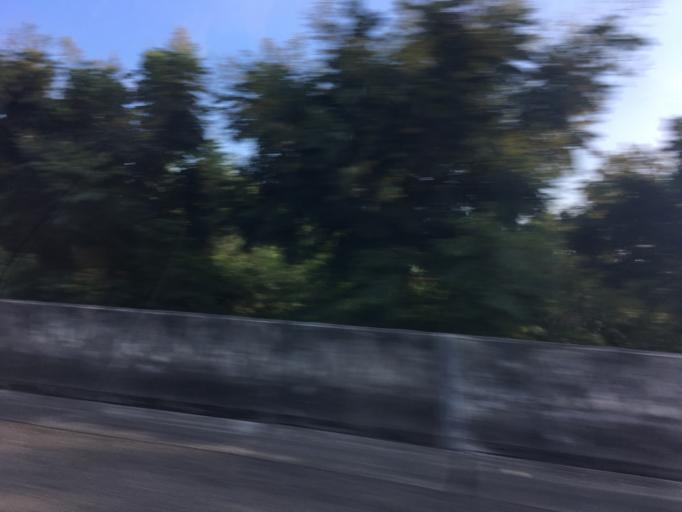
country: TW
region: Taiwan
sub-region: Chiayi
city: Taibao
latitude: 23.4272
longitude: 120.3439
